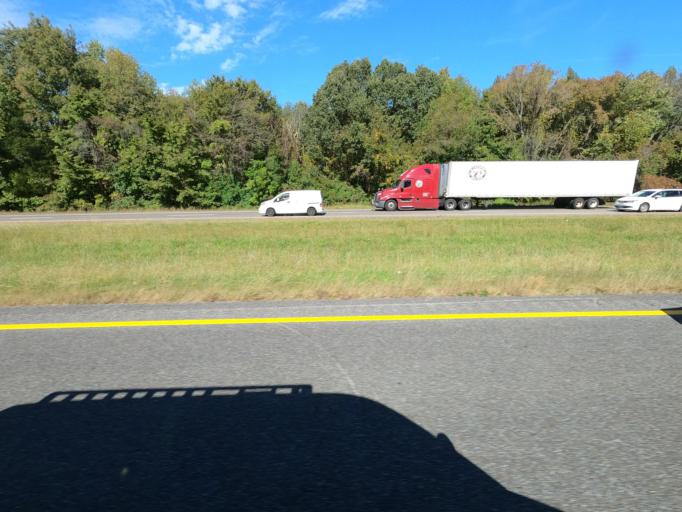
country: US
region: Tennessee
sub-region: Haywood County
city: Brownsville
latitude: 35.4426
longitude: -89.3301
